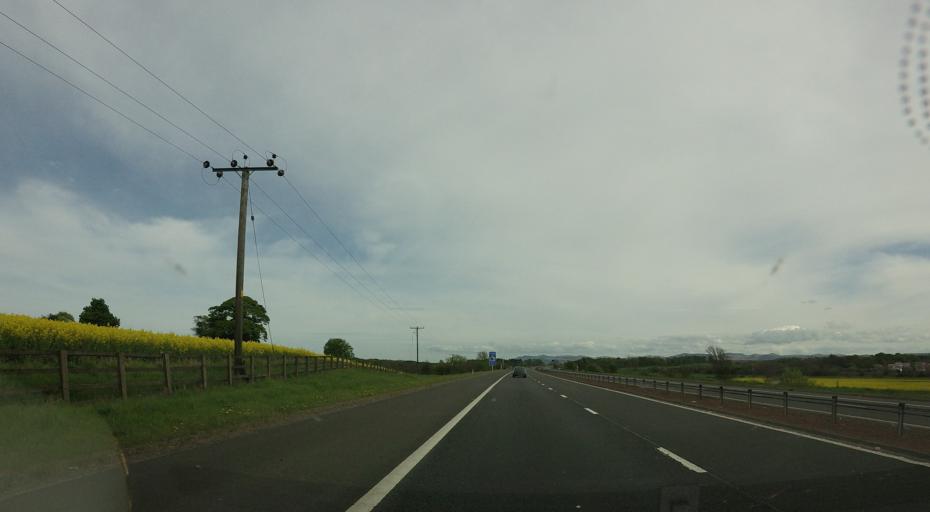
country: GB
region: Scotland
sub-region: West Lothian
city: Broxburn
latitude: 55.9719
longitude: -3.4615
